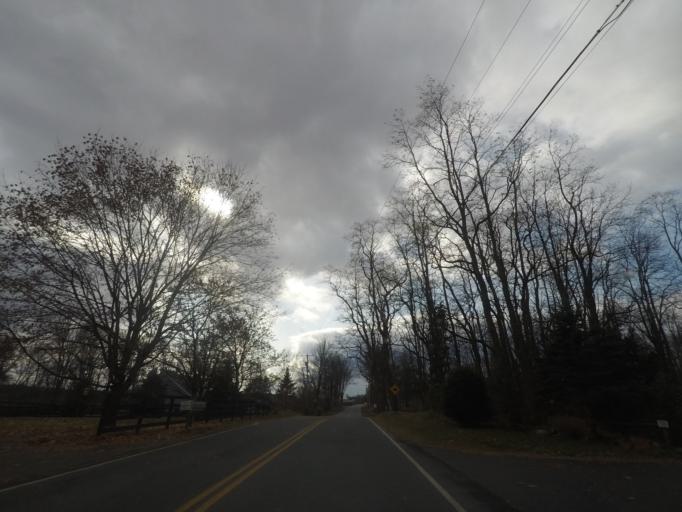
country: US
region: New York
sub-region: Saratoga County
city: Ballston Spa
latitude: 42.9886
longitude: -73.8183
